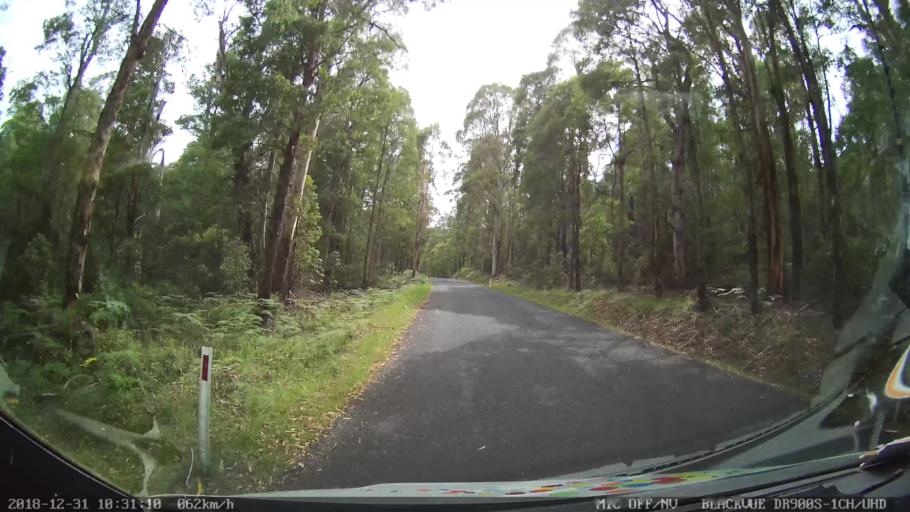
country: AU
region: New South Wales
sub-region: Snowy River
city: Jindabyne
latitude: -36.4594
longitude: 148.1557
